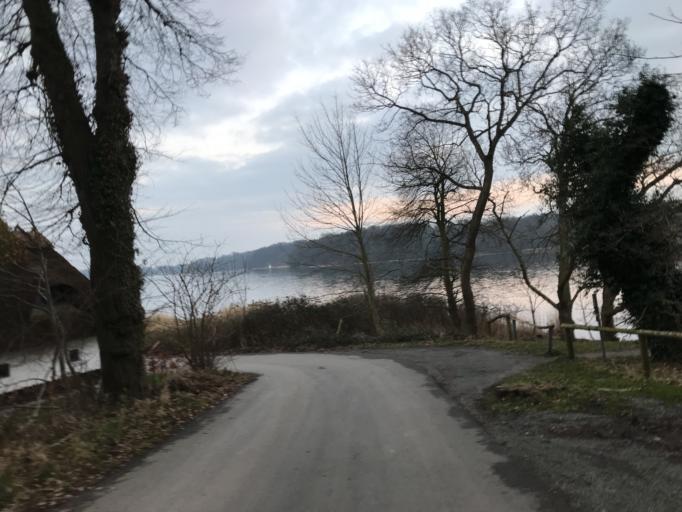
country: DK
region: South Denmark
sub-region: Fredericia Kommune
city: Snoghoj
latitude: 55.5032
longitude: 9.6906
